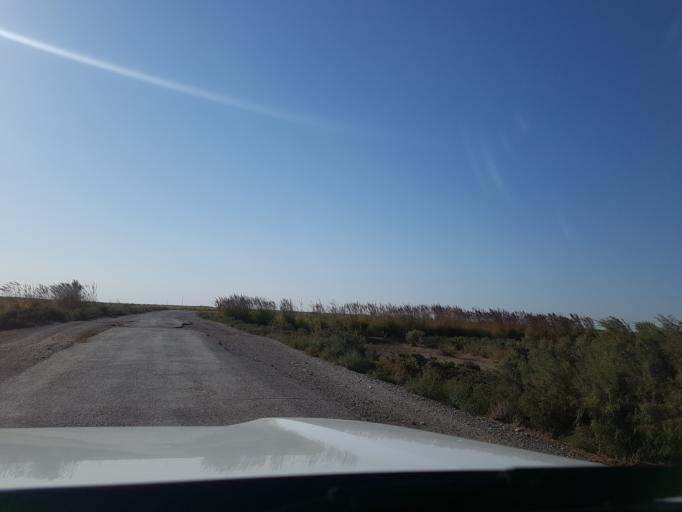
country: IR
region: Razavi Khorasan
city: Sarakhs
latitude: 36.9970
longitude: 61.3834
